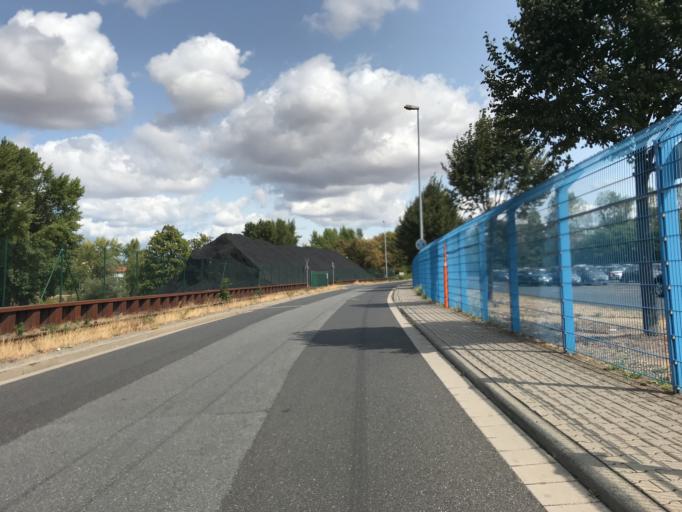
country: DE
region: Hesse
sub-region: Regierungsbezirk Darmstadt
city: Ginsheim-Gustavsburg
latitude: 49.9922
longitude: 8.3152
